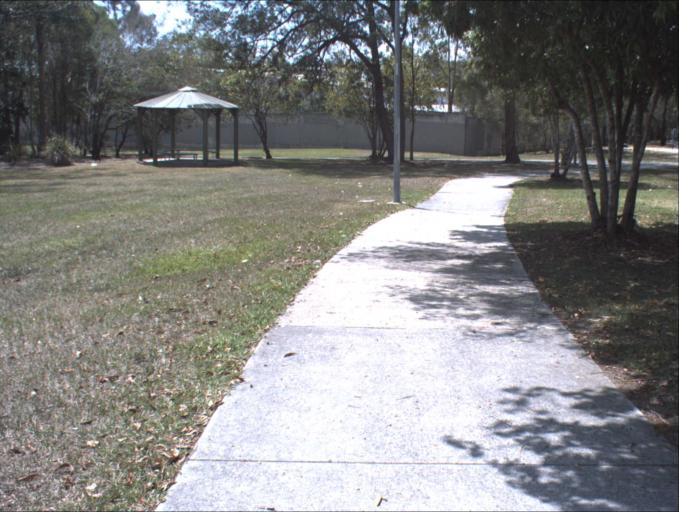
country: AU
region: Queensland
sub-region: Logan
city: Woodridge
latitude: -27.6206
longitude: 153.1021
